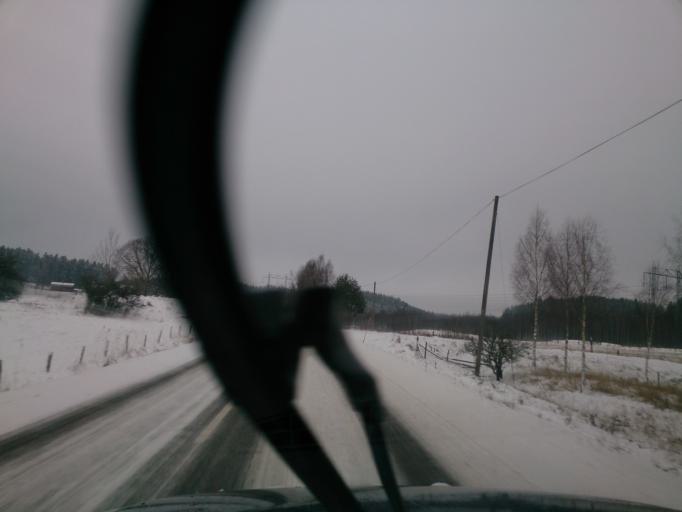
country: SE
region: OEstergoetland
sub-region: Atvidabergs Kommun
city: Atvidaberg
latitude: 58.3455
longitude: 16.0294
